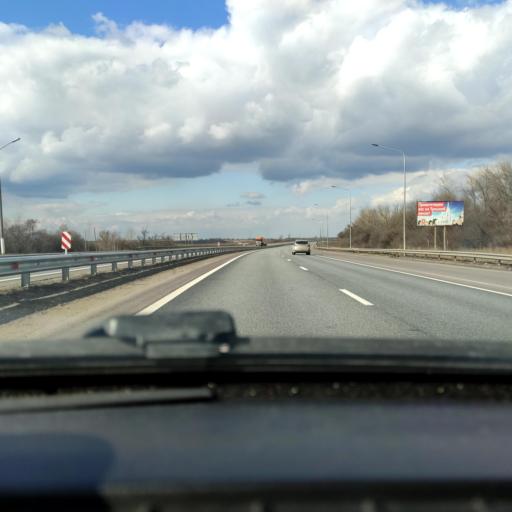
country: RU
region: Tula
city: Yefremov
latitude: 53.0162
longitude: 38.2144
